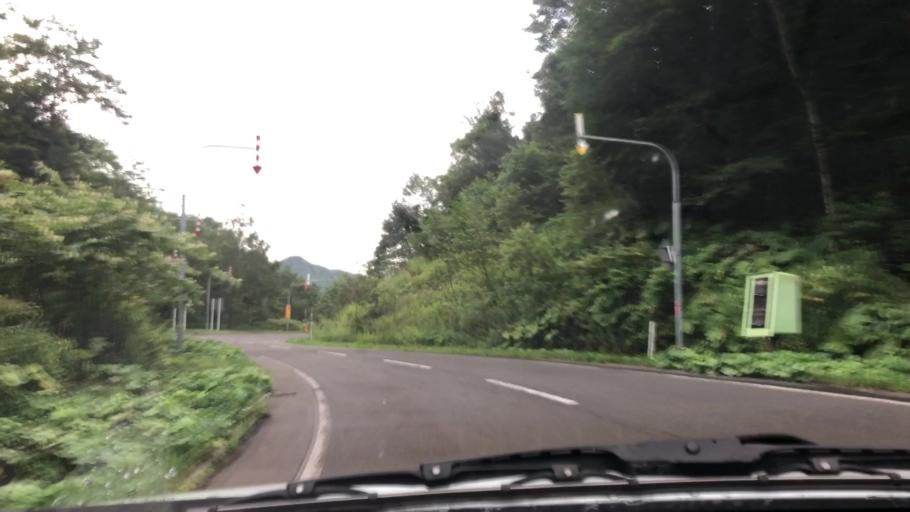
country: JP
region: Hokkaido
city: Shimo-furano
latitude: 42.9337
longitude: 142.3737
